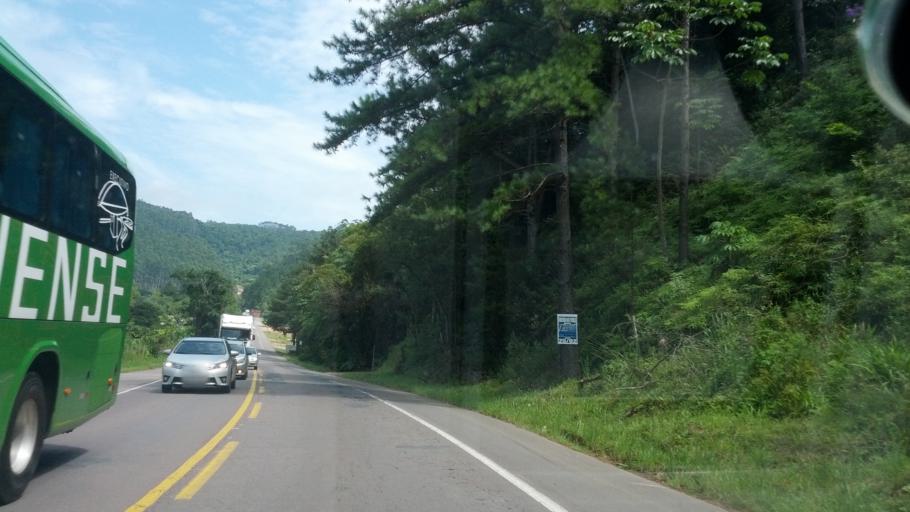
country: BR
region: Santa Catarina
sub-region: Ibirama
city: Ibirama
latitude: -27.0787
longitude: -49.4879
